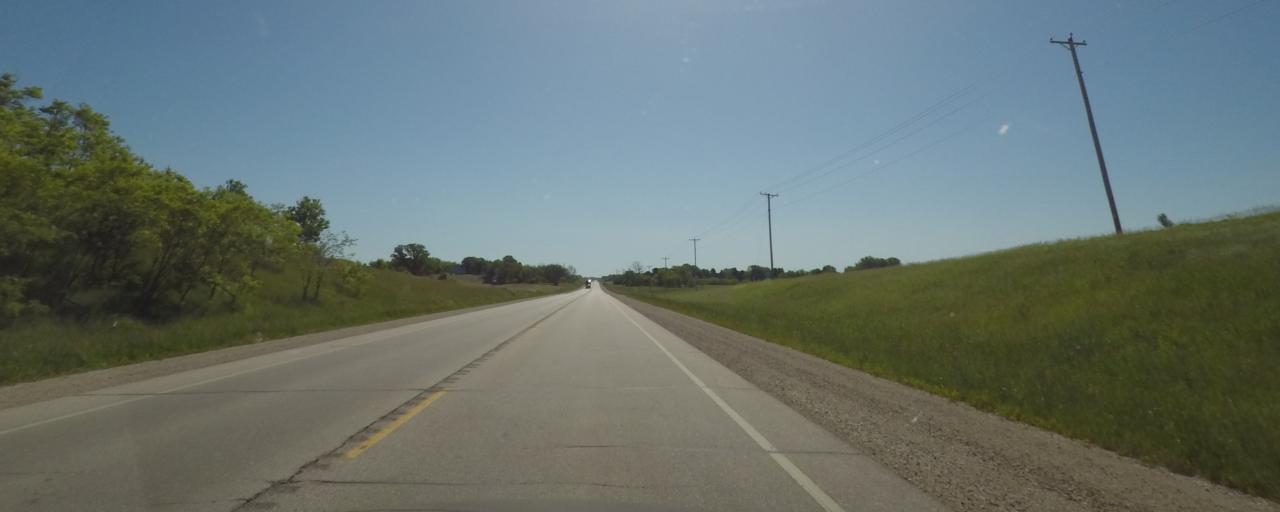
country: US
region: Wisconsin
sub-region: Fond du Lac County
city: Saint Peter
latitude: 43.7834
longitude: -88.3394
